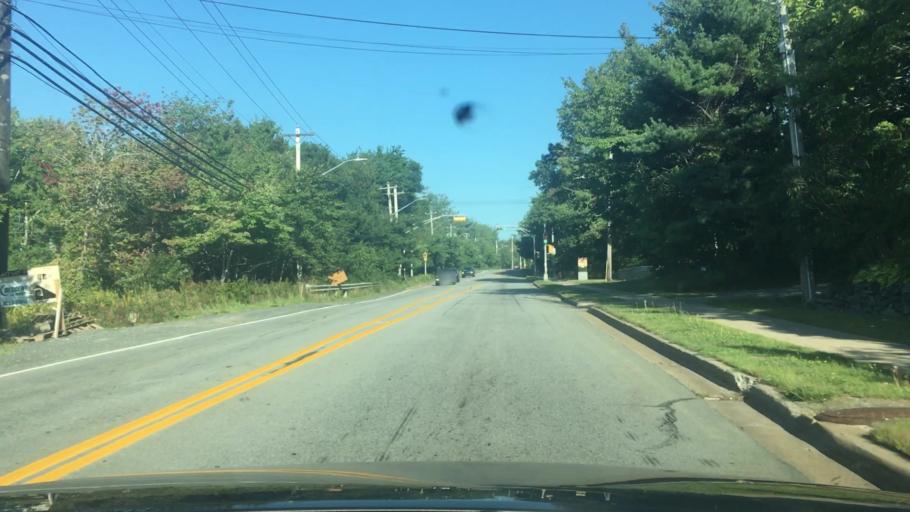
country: CA
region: Nova Scotia
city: Dartmouth
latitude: 44.7165
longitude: -63.6822
